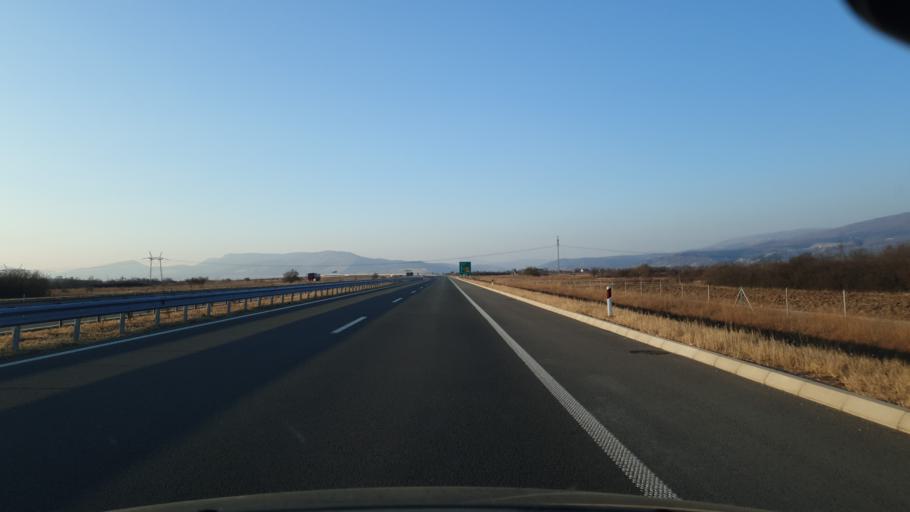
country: RS
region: Central Serbia
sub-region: Pirotski Okrug
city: Pirot
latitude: 43.1101
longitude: 22.6332
